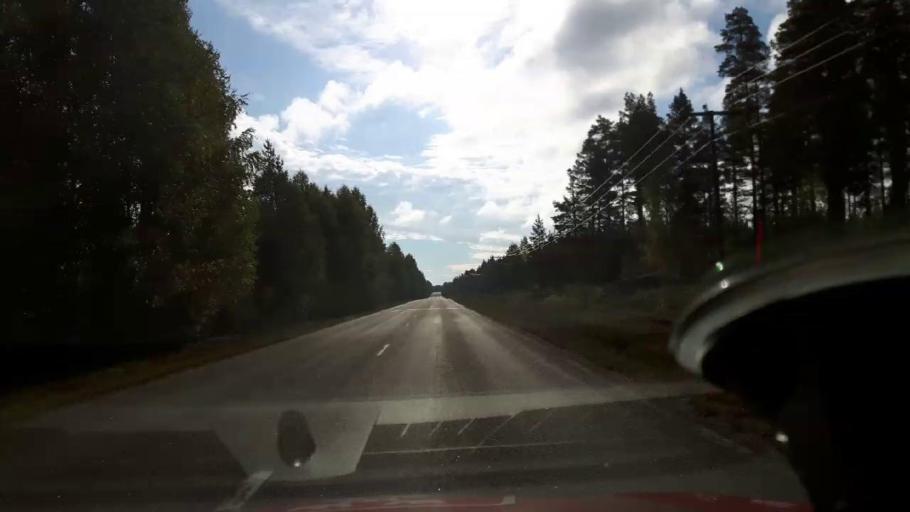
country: SE
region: Jaemtland
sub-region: Harjedalens Kommun
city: Sveg
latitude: 62.1001
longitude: 15.0740
